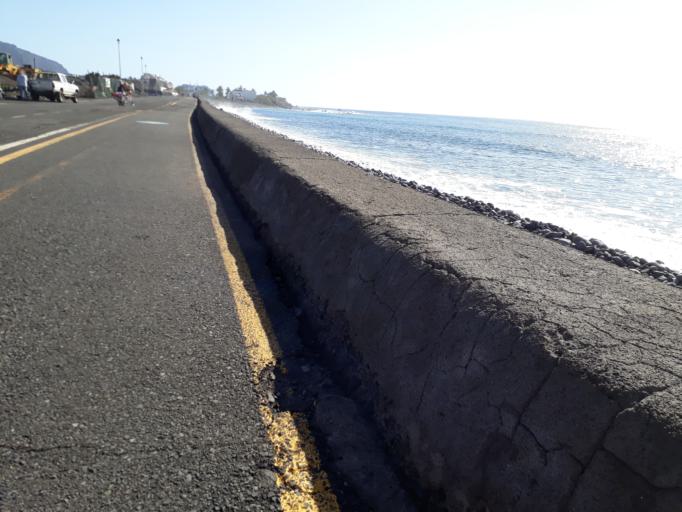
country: ES
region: Canary Islands
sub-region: Provincia de Santa Cruz de Tenerife
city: Alajero
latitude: 28.0930
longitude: -17.3407
